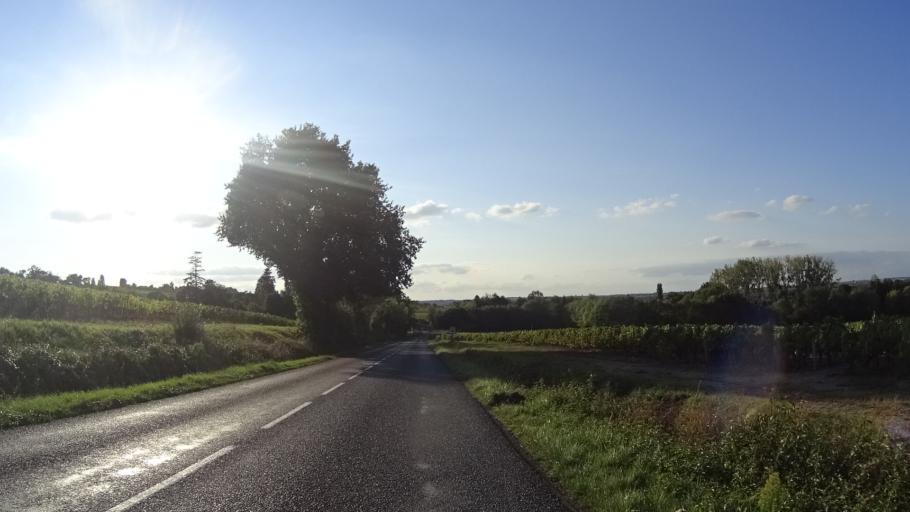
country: FR
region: Pays de la Loire
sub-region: Departement de Maine-et-Loire
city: Lire
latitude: 47.3409
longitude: -1.1403
